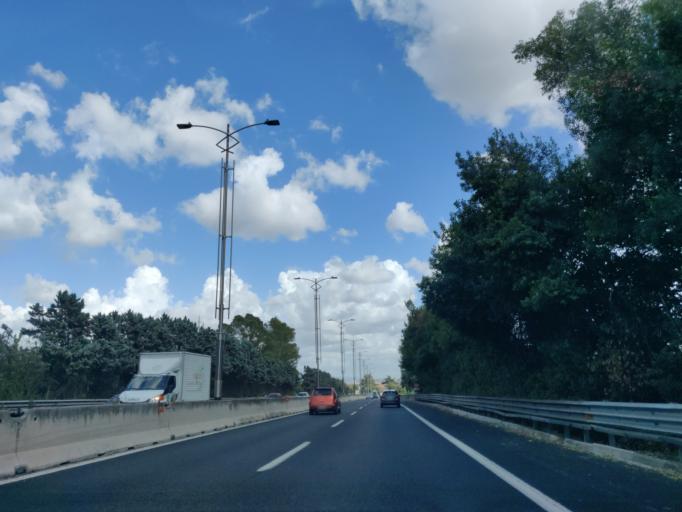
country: IT
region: Latium
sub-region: Citta metropolitana di Roma Capitale
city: Vitinia
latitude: 41.8334
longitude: 12.4300
